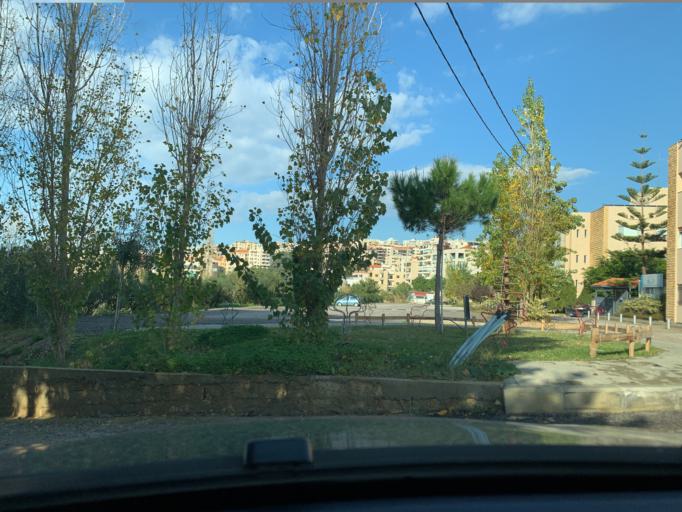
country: LB
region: Mont-Liban
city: Baabda
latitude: 33.8499
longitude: 35.5660
